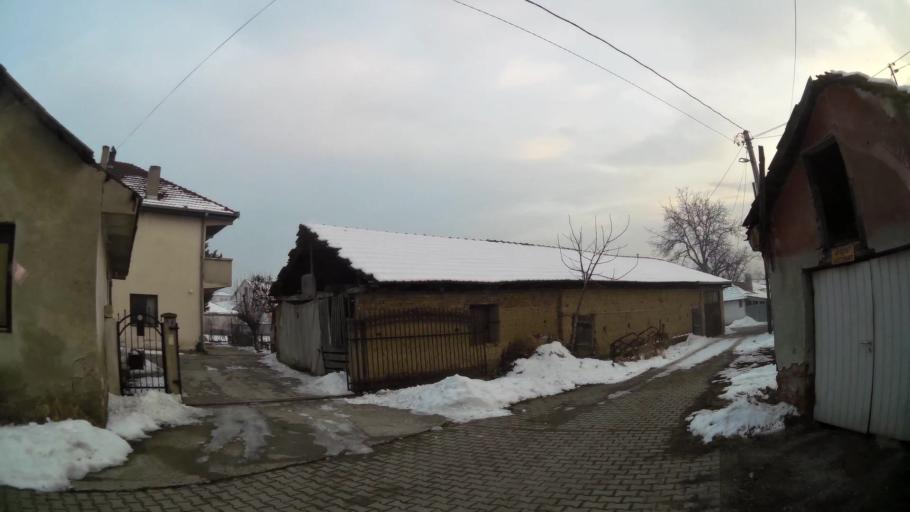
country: MK
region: Suto Orizari
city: Suto Orizare
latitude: 42.0362
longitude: 21.4085
